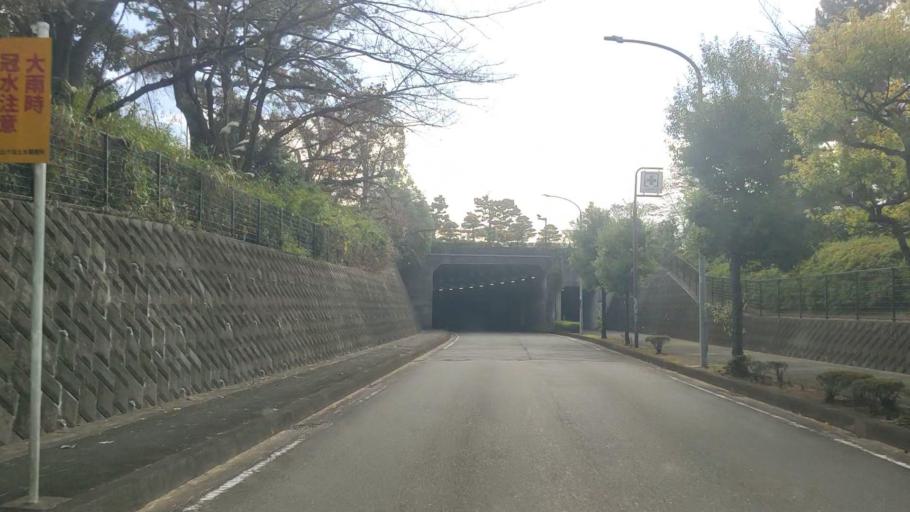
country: JP
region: Kanagawa
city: Yokohama
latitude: 35.4464
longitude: 139.5496
